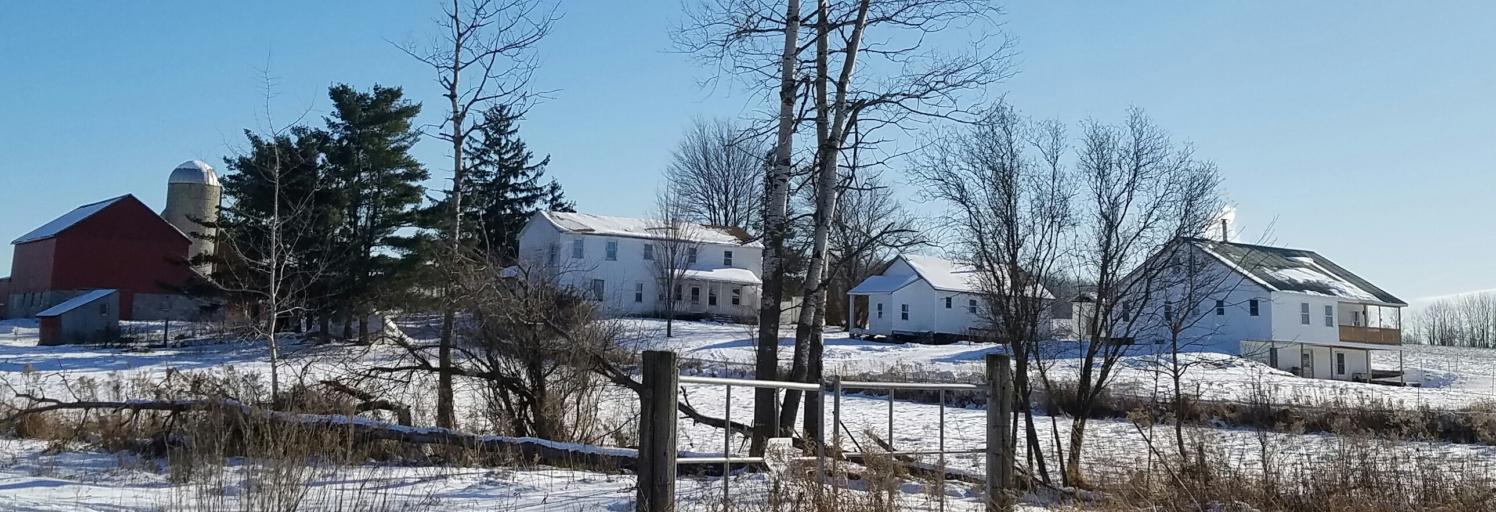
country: US
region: Wisconsin
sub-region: Clark County
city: Loyal
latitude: 44.5911
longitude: -90.4360
